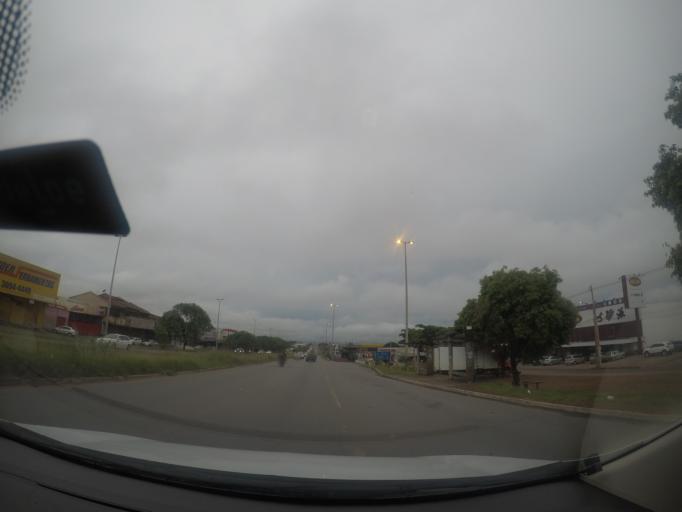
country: BR
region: Goias
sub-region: Aparecida De Goiania
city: Aparecida de Goiania
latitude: -16.7626
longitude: -49.3468
